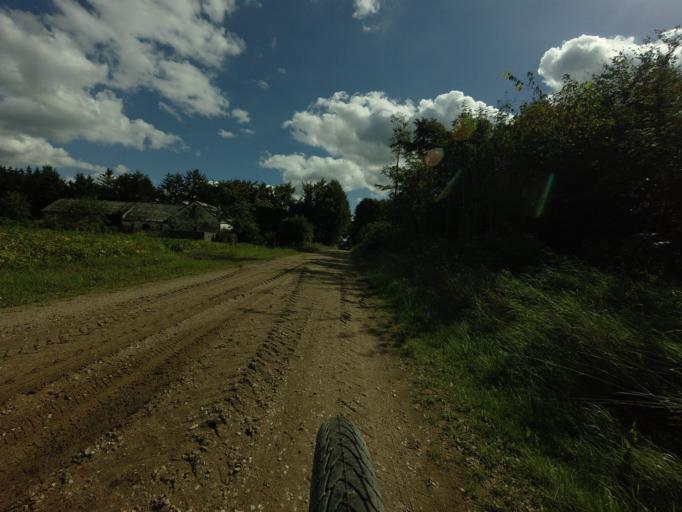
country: DK
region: Central Jutland
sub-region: Ikast-Brande Kommune
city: Brande
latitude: 55.9719
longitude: 9.1539
